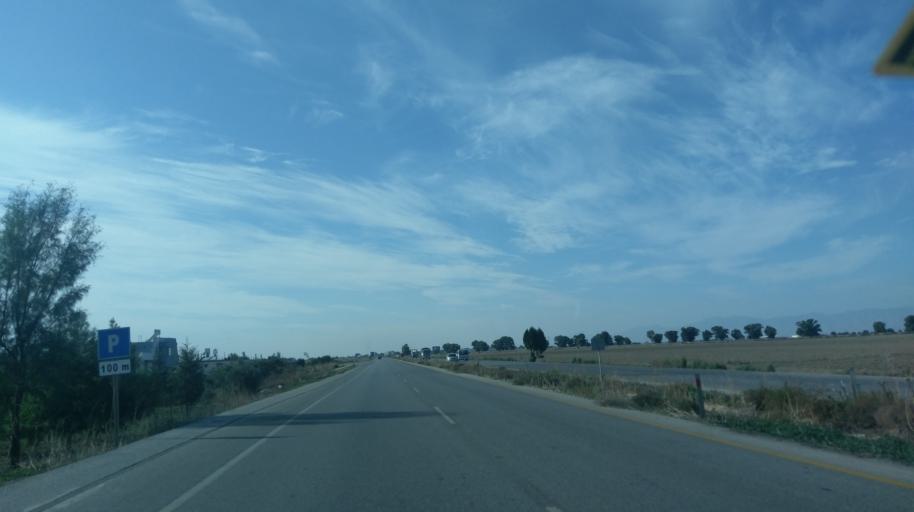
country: CY
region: Ammochostos
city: Lefkonoiko
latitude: 35.1711
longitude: 33.7841
